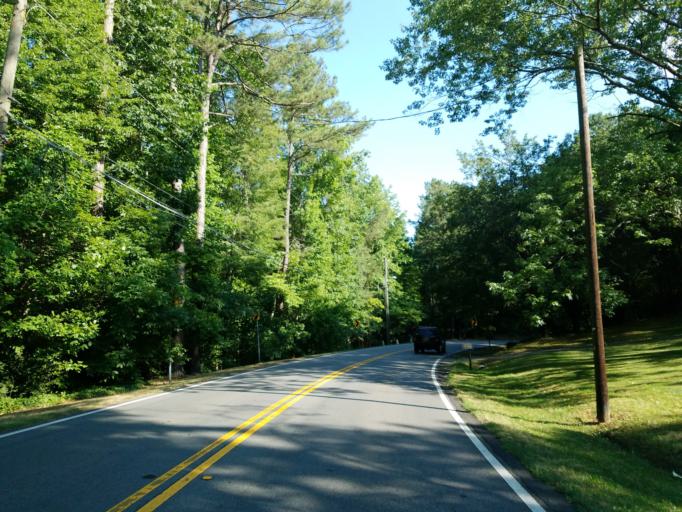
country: US
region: Georgia
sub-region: Fulton County
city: Milton
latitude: 34.1143
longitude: -84.3380
